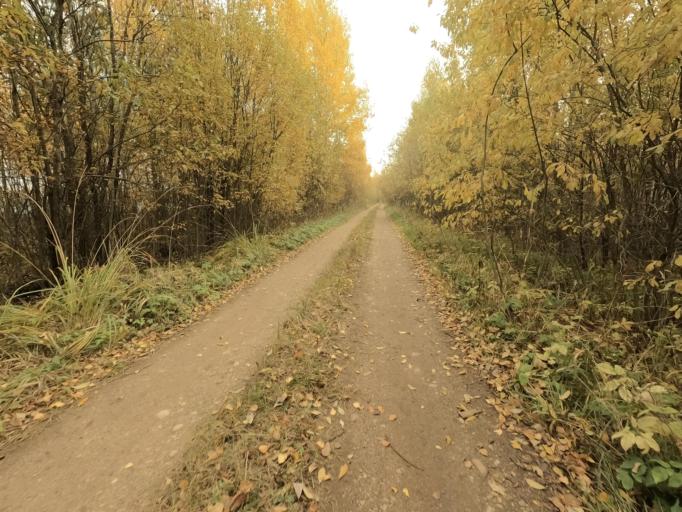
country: RU
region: Novgorod
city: Pankovka
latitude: 58.8749
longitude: 30.8782
